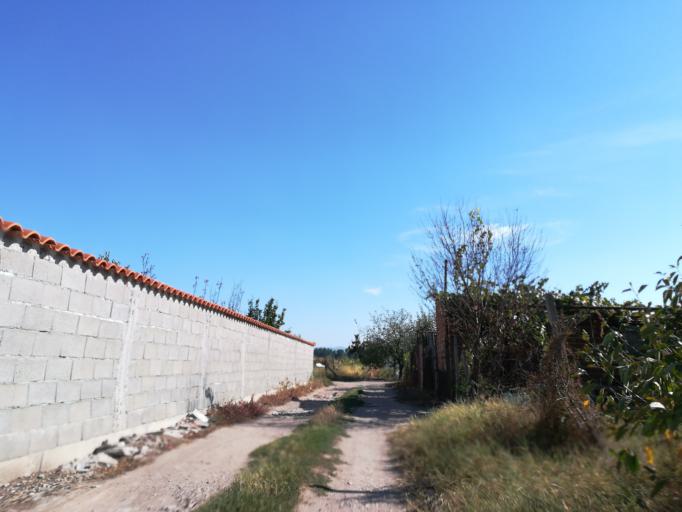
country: BG
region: Stara Zagora
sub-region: Obshtina Chirpan
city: Chirpan
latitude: 42.0935
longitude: 25.2313
